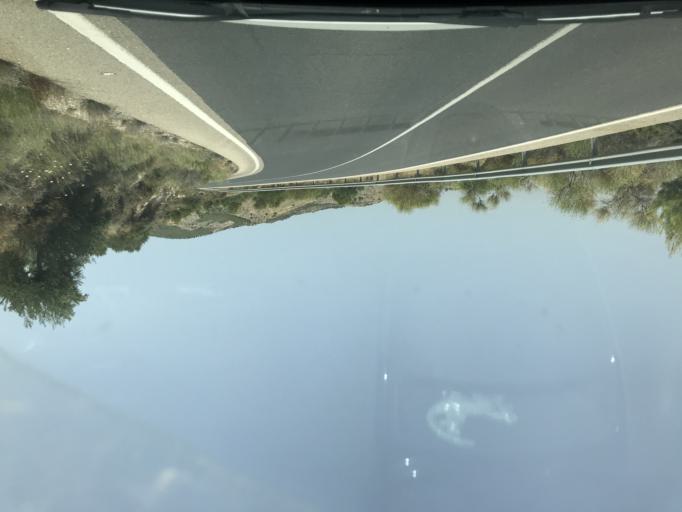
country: ES
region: Castille-La Mancha
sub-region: Provincia de Cuenca
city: Albalate de las Nogueras
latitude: 40.3824
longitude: -2.2744
